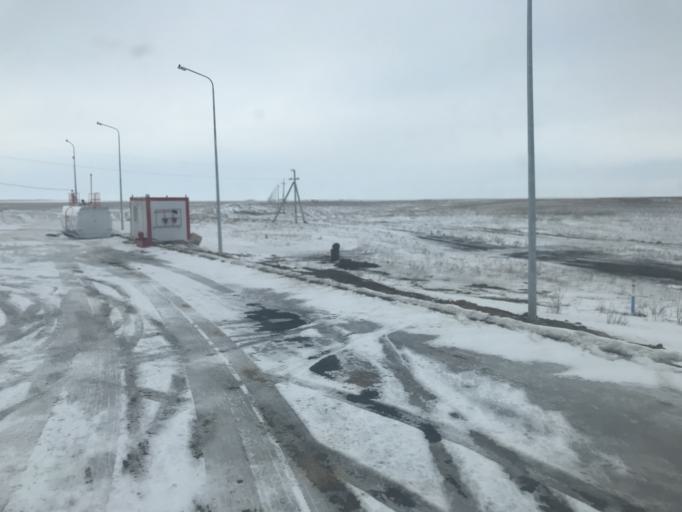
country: KZ
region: Batys Qazaqstan
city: Oral
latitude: 51.4041
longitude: 51.2980
